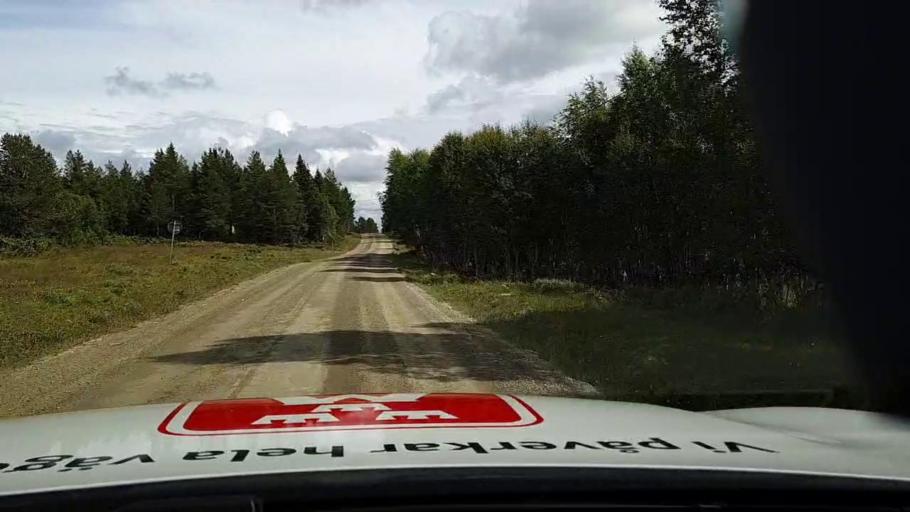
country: SE
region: Jaemtland
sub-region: Are Kommun
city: Jarpen
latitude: 62.5512
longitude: 13.4465
